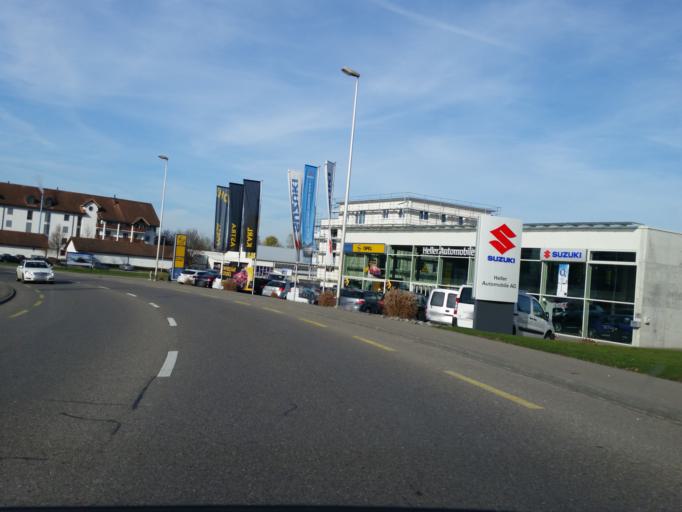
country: CH
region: Thurgau
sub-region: Kreuzlingen District
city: Bottighofen
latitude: 47.6408
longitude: 9.2003
